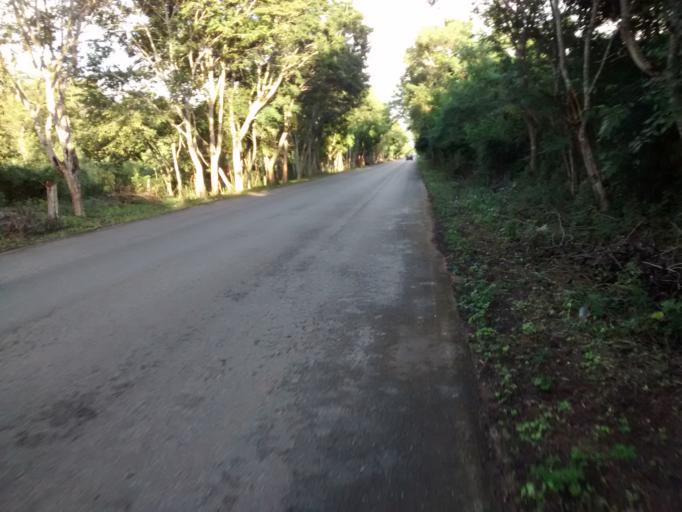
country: MX
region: Yucatan
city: Valladolid
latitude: 20.7312
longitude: -88.2223
